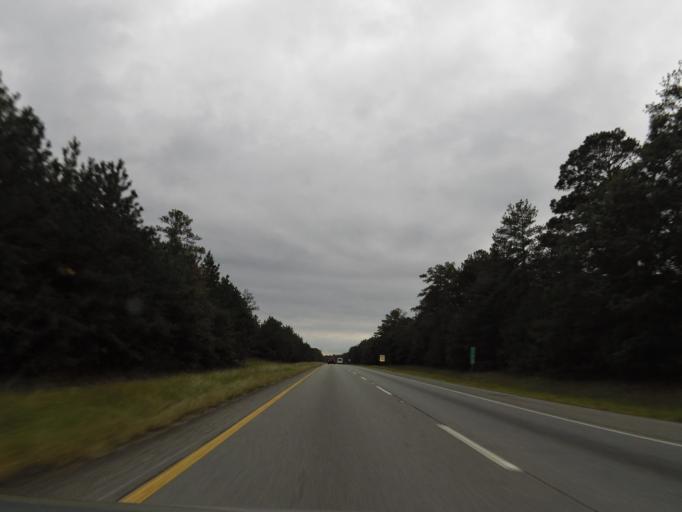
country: US
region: Alabama
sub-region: Saint Clair County
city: Steele
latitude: 33.9283
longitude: -86.2014
